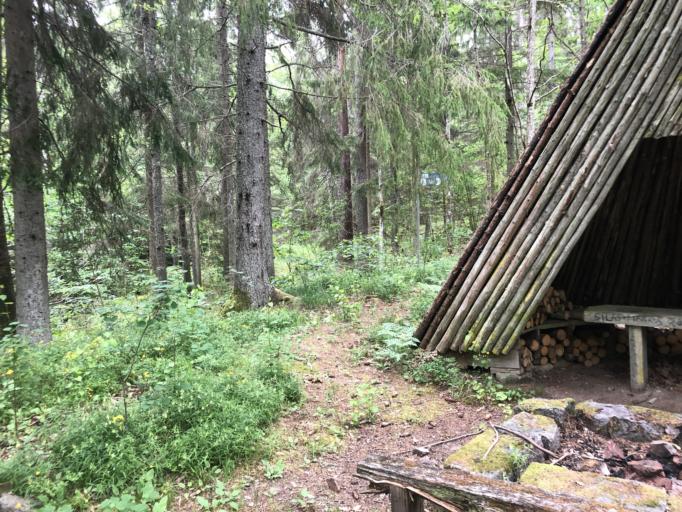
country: SE
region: Kalmar
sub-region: Oskarshamns Kommun
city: Oskarshamn
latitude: 57.4897
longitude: 16.4762
